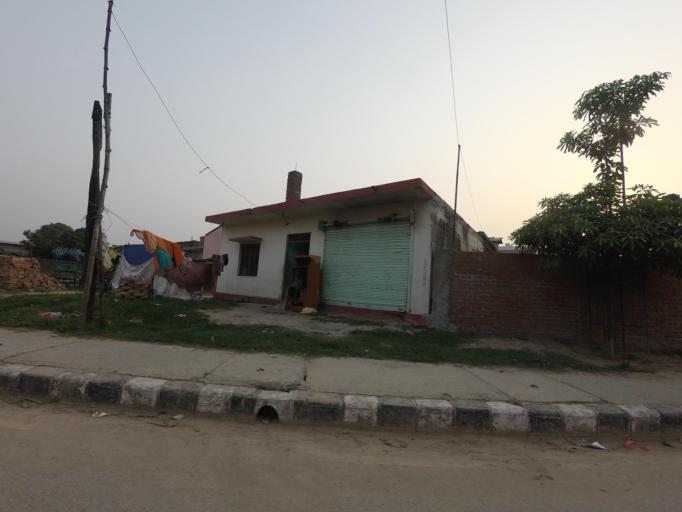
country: NP
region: Western Region
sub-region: Lumbini Zone
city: Bhairahawa
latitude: 27.5098
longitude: 83.4636
